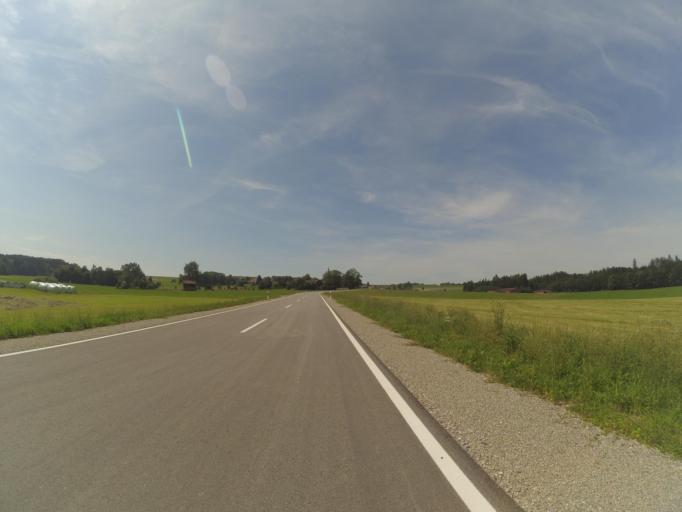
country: DE
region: Bavaria
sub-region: Swabia
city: Unteregg
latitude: 47.9643
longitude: 10.4772
